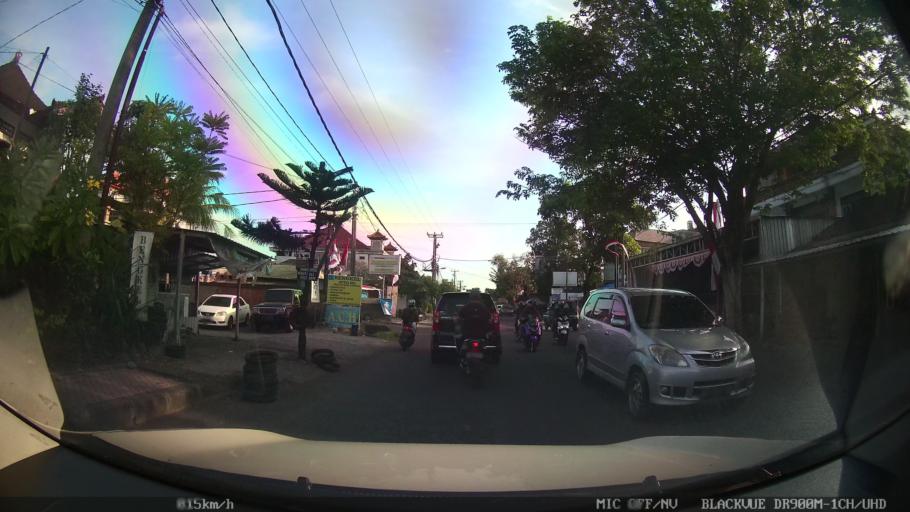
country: ID
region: Bali
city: Banjar Kertasari
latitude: -8.6234
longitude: 115.2094
